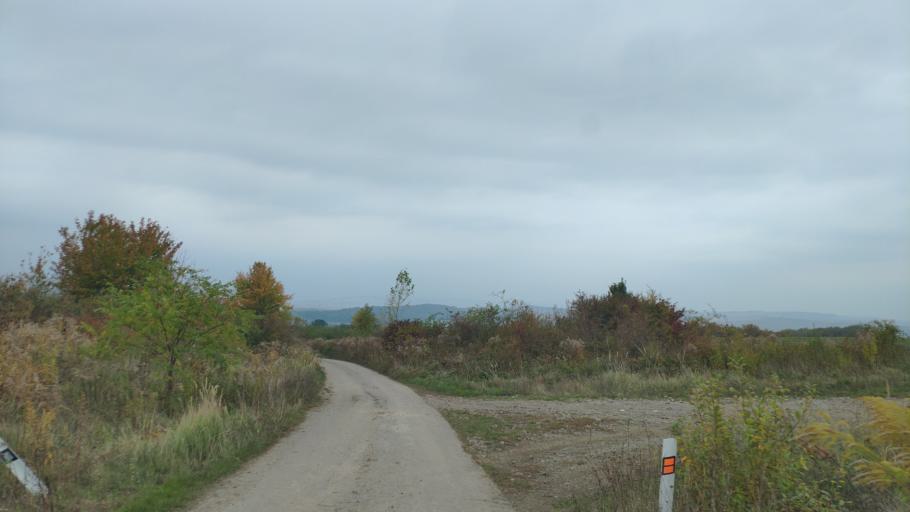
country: SK
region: Kosicky
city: Kosice
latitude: 48.6288
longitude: 21.4057
